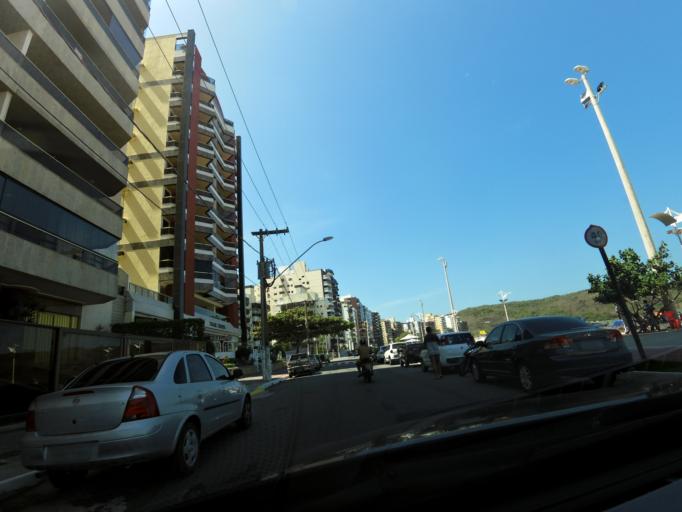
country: BR
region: Espirito Santo
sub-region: Guarapari
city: Guarapari
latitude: -20.6521
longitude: -40.4800
